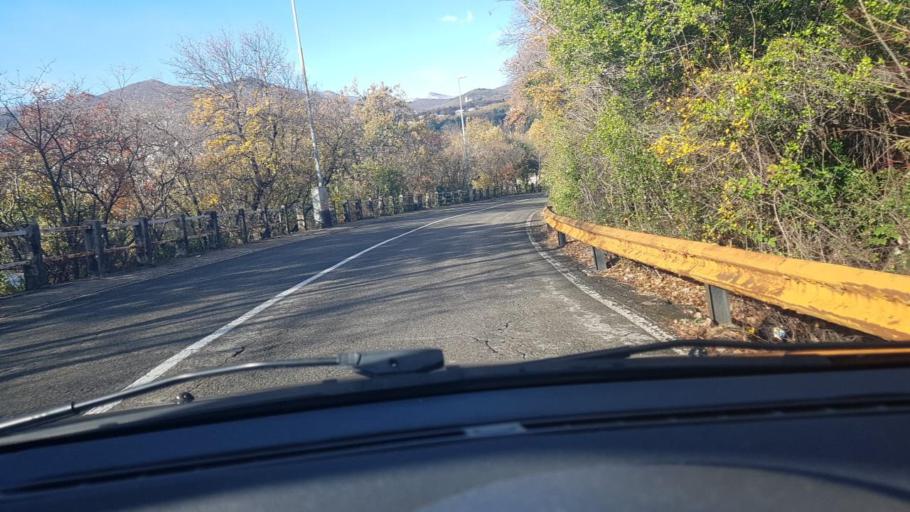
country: HR
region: Primorsko-Goranska
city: Matulji
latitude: 45.3508
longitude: 14.3387
